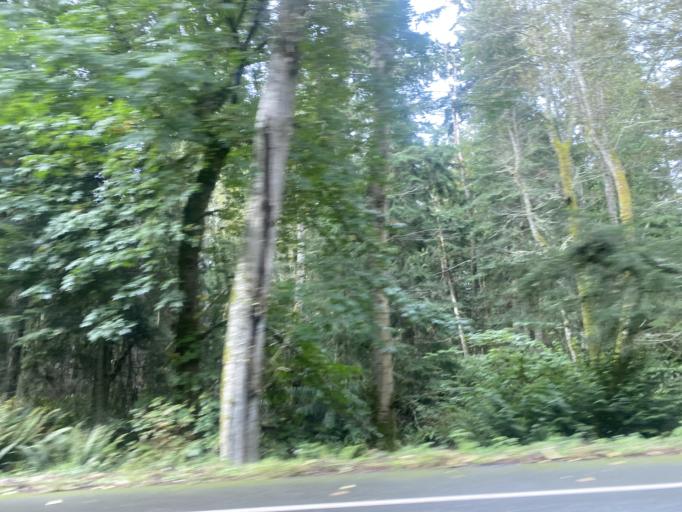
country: US
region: Washington
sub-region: Island County
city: Freeland
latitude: 48.0480
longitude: -122.5067
